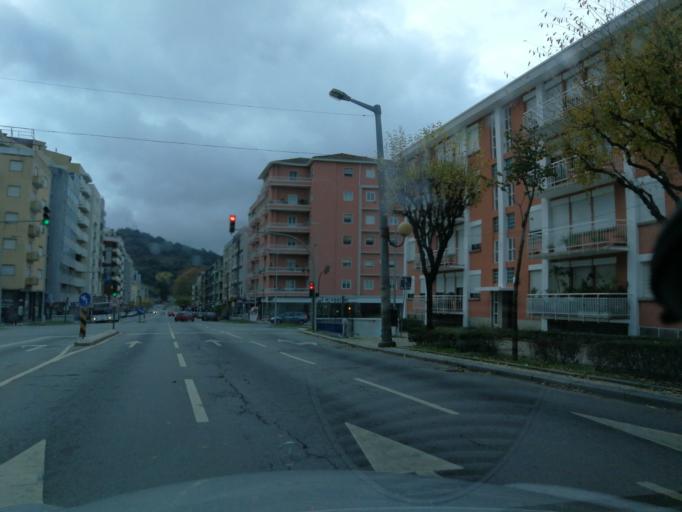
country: PT
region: Braga
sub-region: Braga
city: Braga
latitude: 41.5464
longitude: -8.4201
